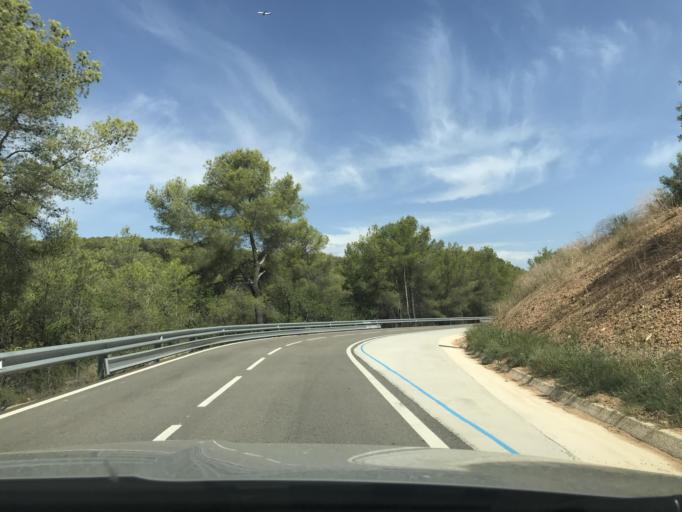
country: ES
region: Catalonia
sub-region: Provincia de Tarragona
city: Salomo
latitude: 41.1948
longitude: 1.3840
